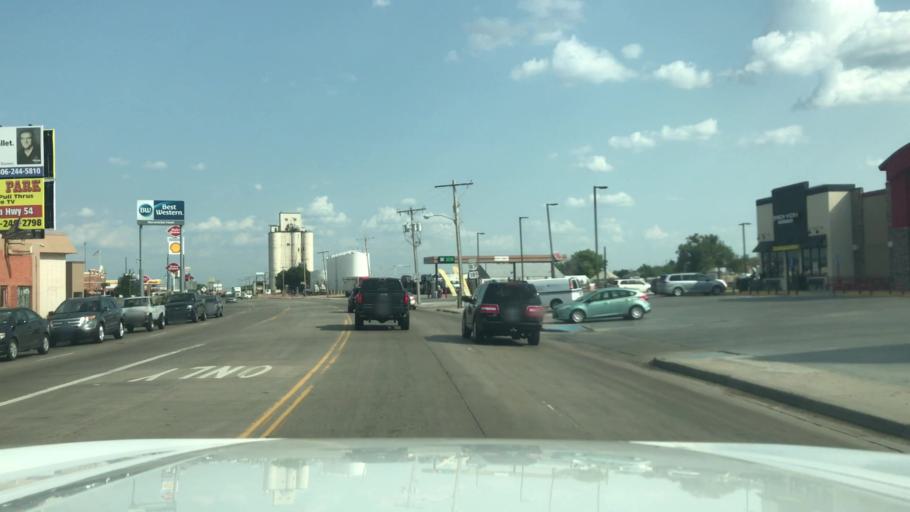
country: US
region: Texas
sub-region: Dallam County
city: Dalhart
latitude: 36.0649
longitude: -102.5208
